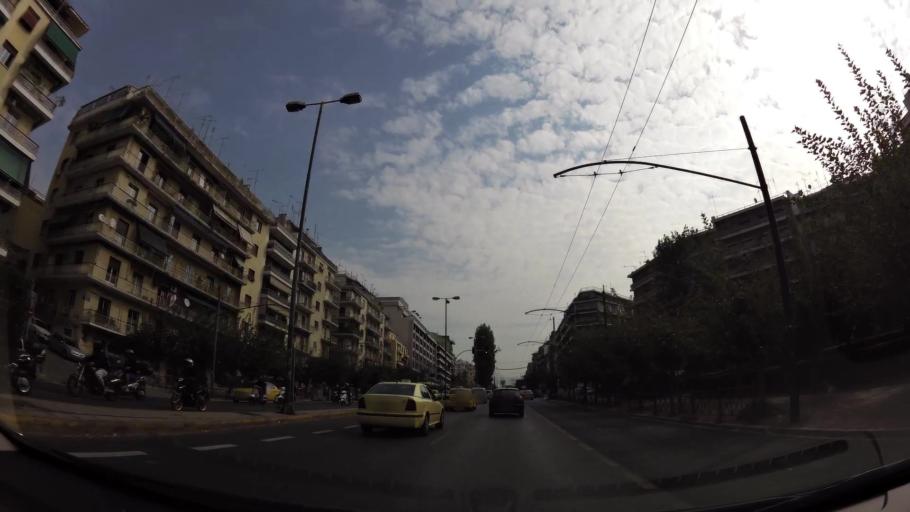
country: GR
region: Attica
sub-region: Nomarchia Athinas
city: Kipseli
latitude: 37.9895
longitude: 23.7449
